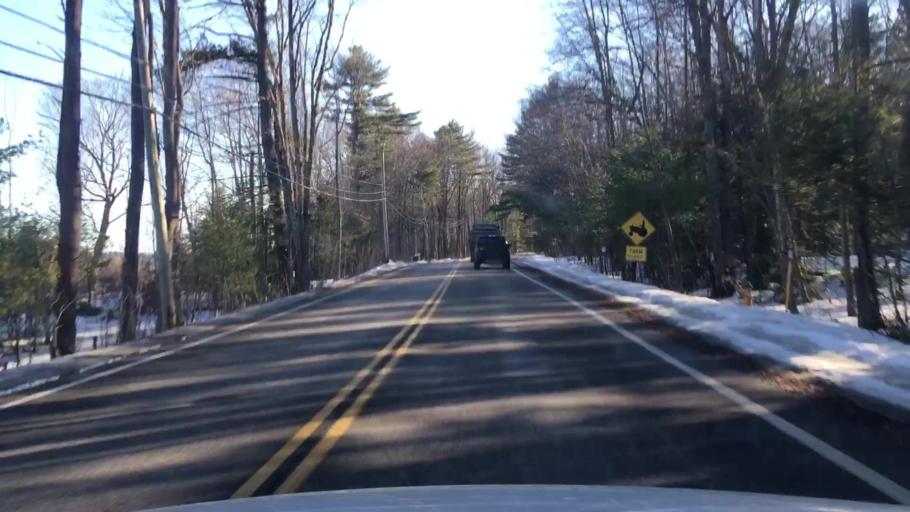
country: US
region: Maine
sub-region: Cumberland County
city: Westbrook
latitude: 43.6998
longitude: -70.3571
